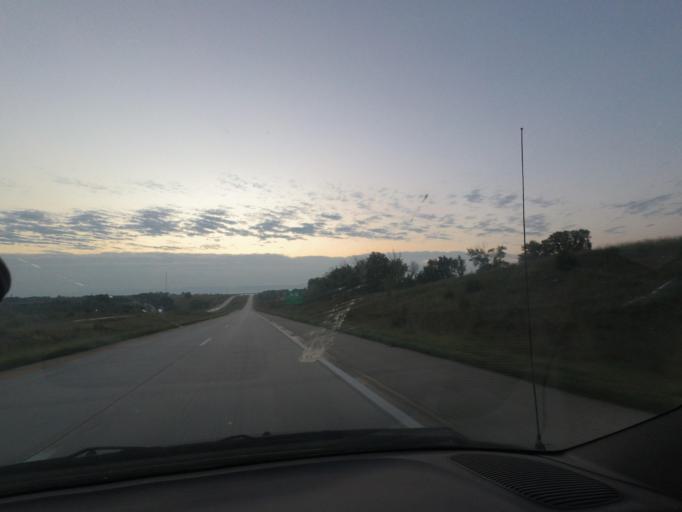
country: US
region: Missouri
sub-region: Linn County
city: Marceline
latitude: 39.7649
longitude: -92.7663
